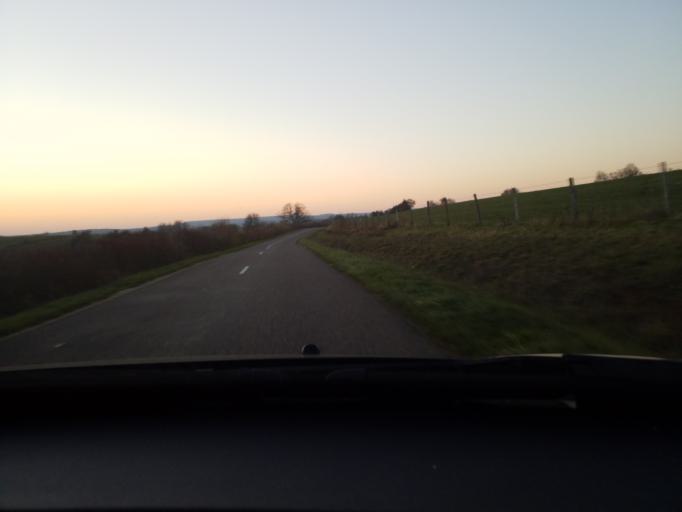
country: FR
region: Franche-Comte
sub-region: Departement de la Haute-Saone
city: Faverney
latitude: 47.8830
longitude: 6.1419
